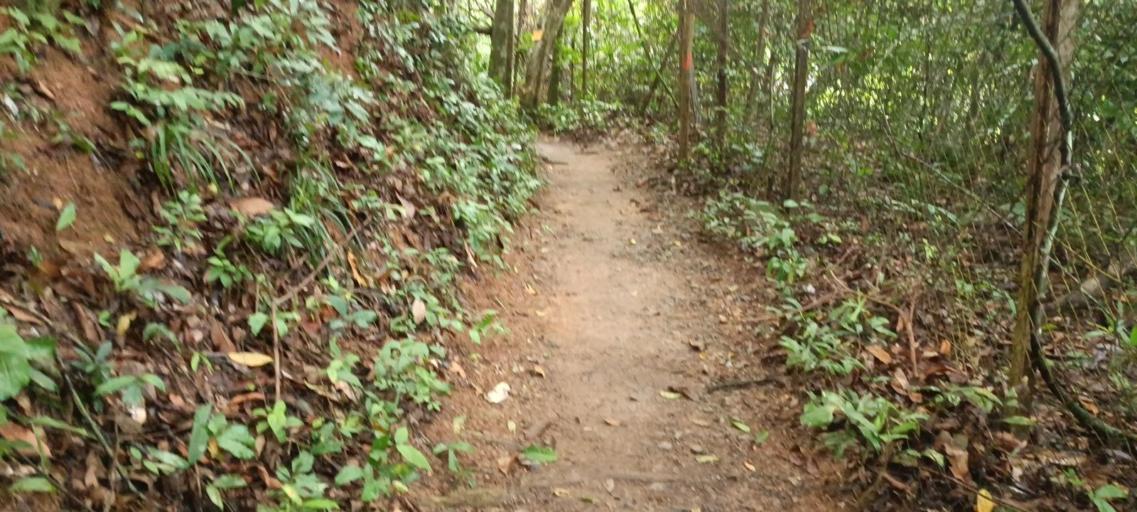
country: MY
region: Penang
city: Bukit Mertajam
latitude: 5.3578
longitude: 100.4917
